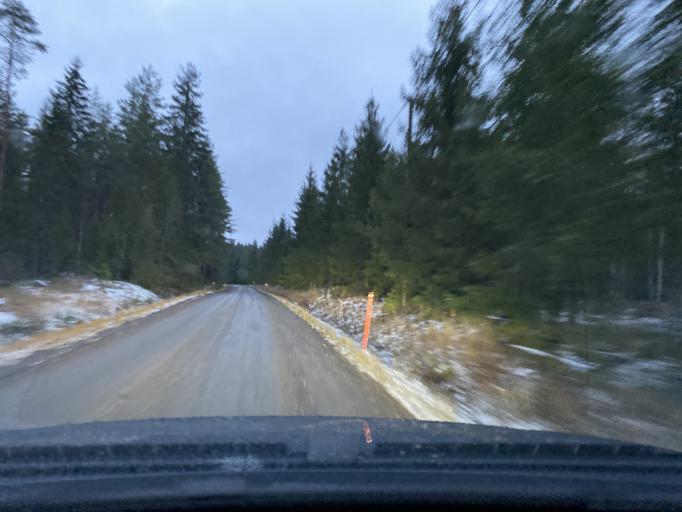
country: FI
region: Pirkanmaa
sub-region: Lounais-Pirkanmaa
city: Punkalaidun
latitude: 61.1470
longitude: 22.9510
